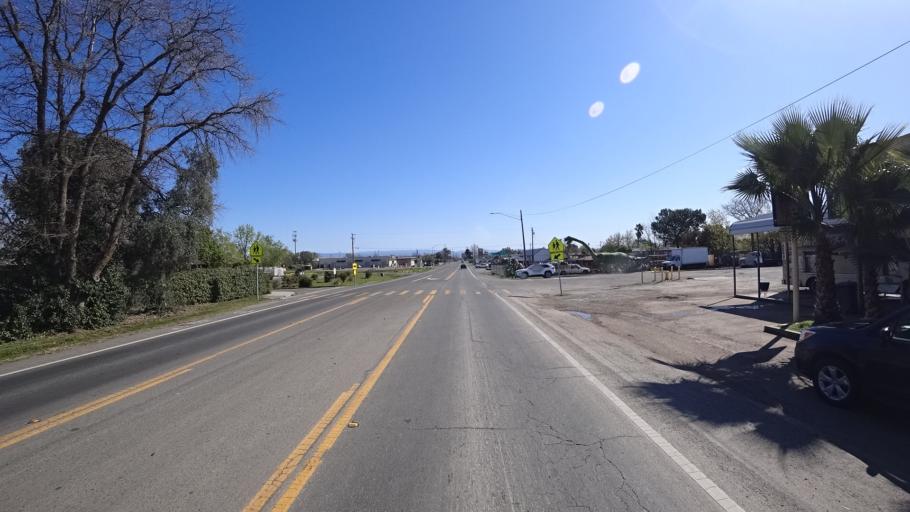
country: US
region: California
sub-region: Glenn County
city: Hamilton City
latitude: 39.7451
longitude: -122.0172
